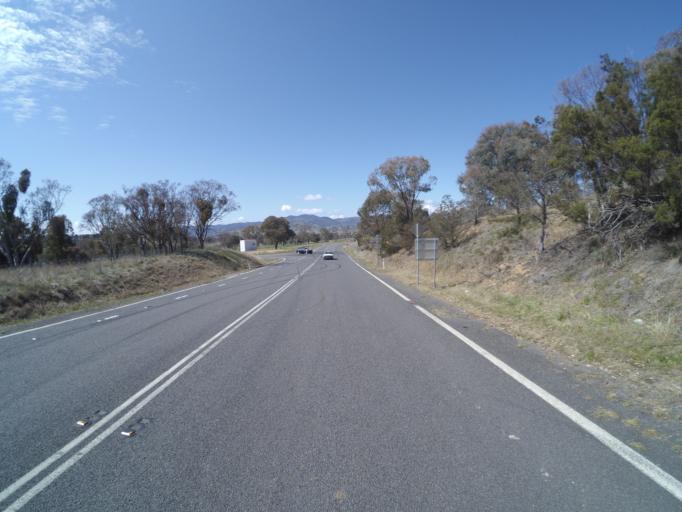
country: AU
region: Australian Capital Territory
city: Macarthur
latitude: -35.4580
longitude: 149.0387
